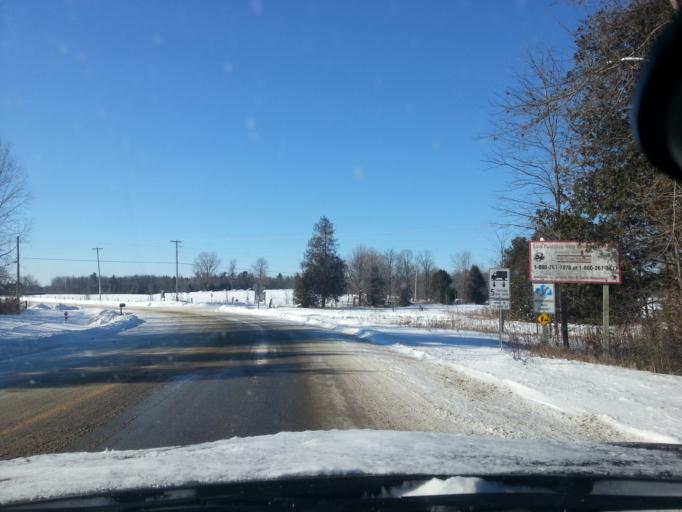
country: CA
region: Ontario
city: Arnprior
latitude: 45.2889
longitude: -76.2896
